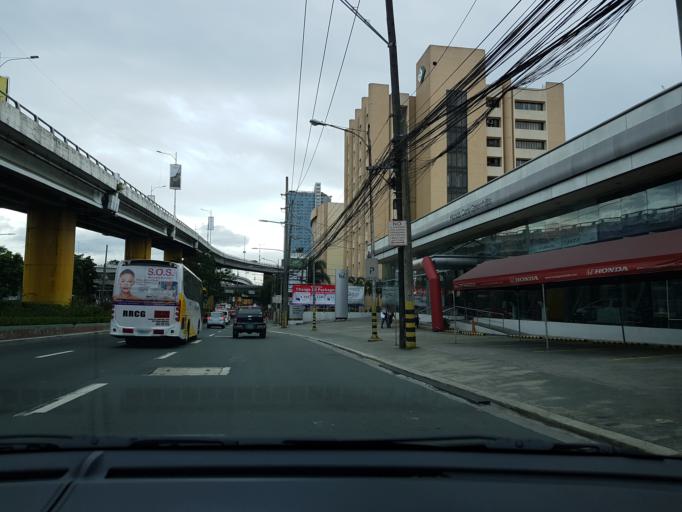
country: PH
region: Metro Manila
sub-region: Pasig
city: Pasig City
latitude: 14.5944
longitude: 121.0567
